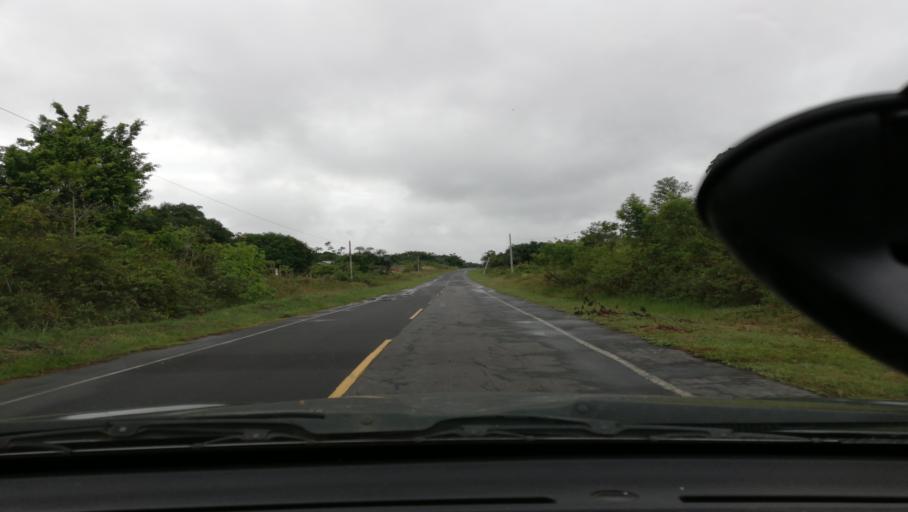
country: PE
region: Loreto
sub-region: Provincia de Loreto
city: Nauta
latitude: -4.3381
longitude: -73.5370
